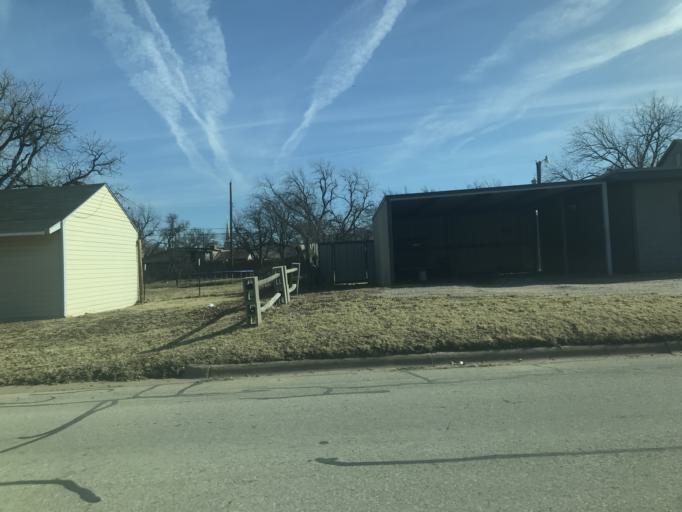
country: US
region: Texas
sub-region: Taylor County
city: Abilene
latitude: 32.4865
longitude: -99.7393
